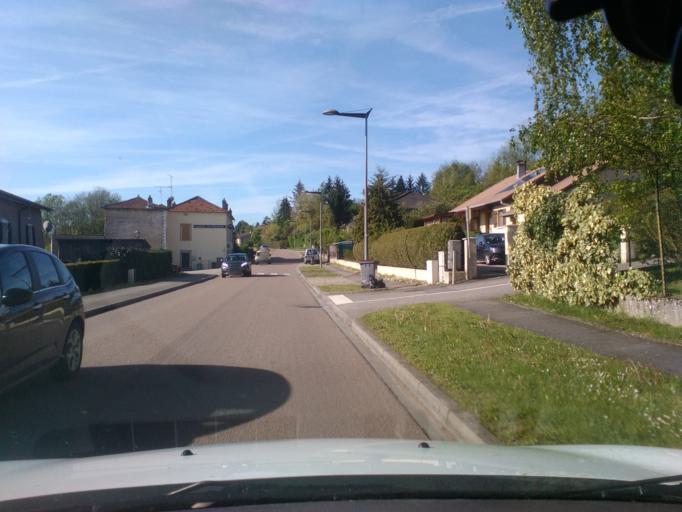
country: FR
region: Lorraine
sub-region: Departement des Vosges
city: Mirecourt
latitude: 48.3190
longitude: 6.1254
